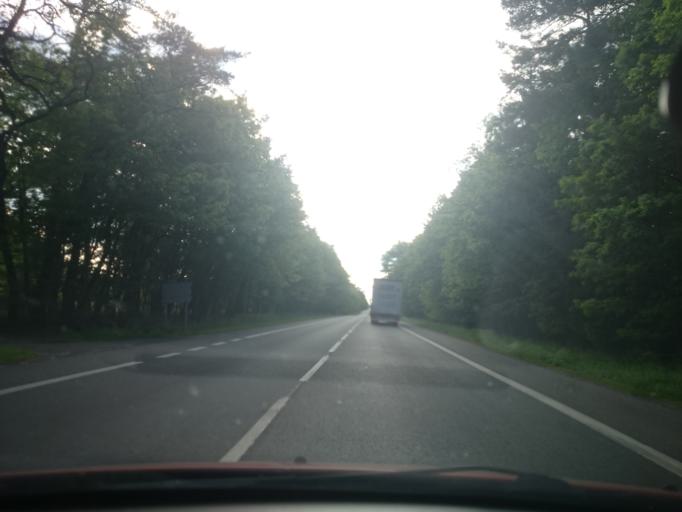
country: PL
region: Opole Voivodeship
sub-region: Powiat opolski
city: Chrzastowice
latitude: 50.6224
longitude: 18.0528
